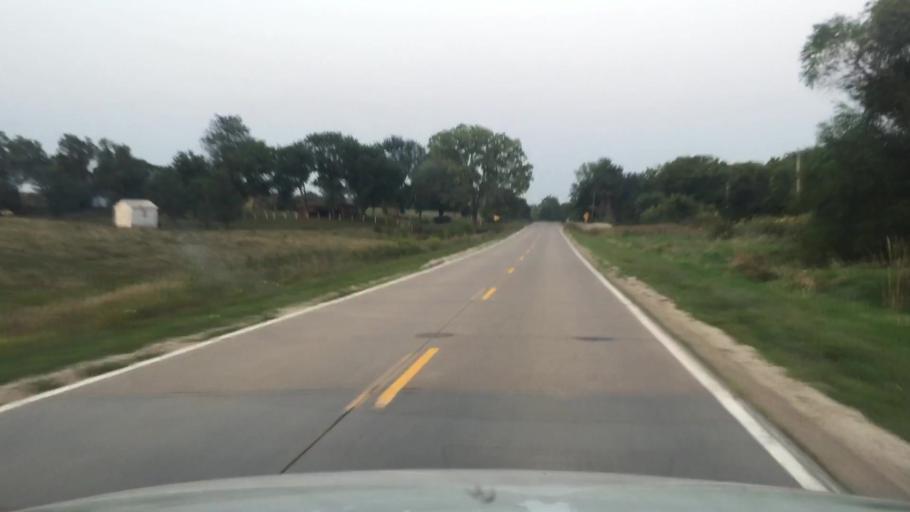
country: US
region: Iowa
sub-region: Clarke County
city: Osceola
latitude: 41.1802
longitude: -93.7181
